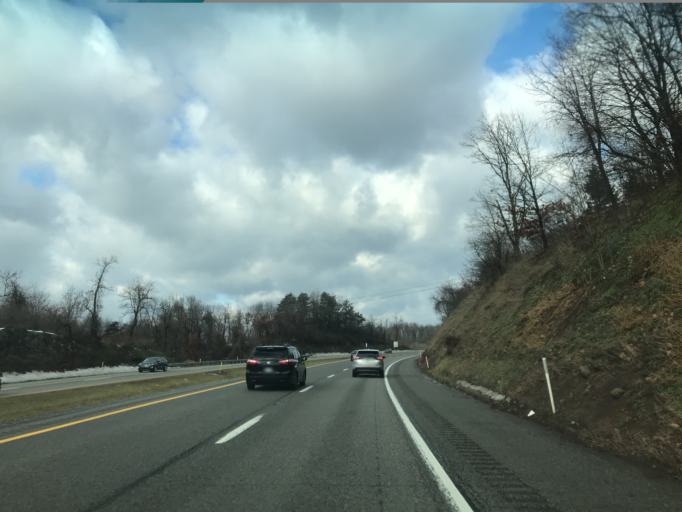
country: US
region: Pennsylvania
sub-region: Bedford County
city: Earlston
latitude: 39.9556
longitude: -78.2438
